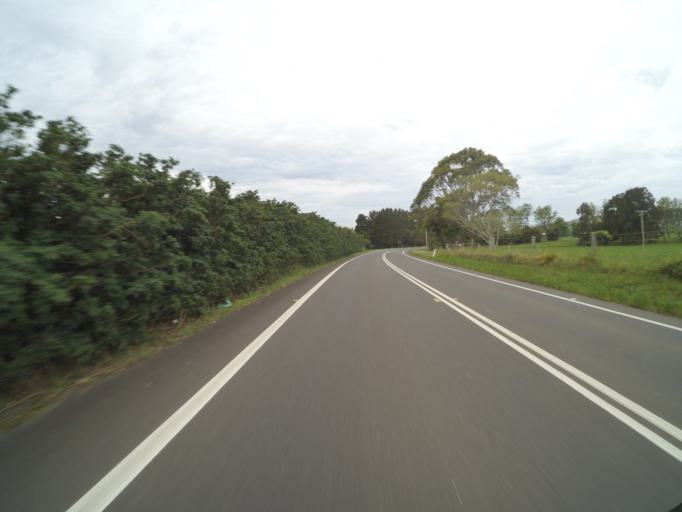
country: AU
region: New South Wales
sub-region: Kiama
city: Jamberoo
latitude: -34.6486
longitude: 150.7882
